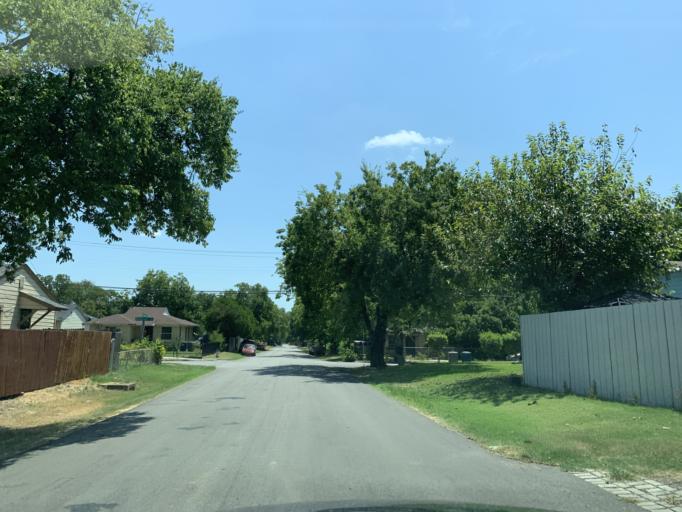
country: US
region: Texas
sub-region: Dallas County
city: Dallas
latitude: 32.6917
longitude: -96.8039
